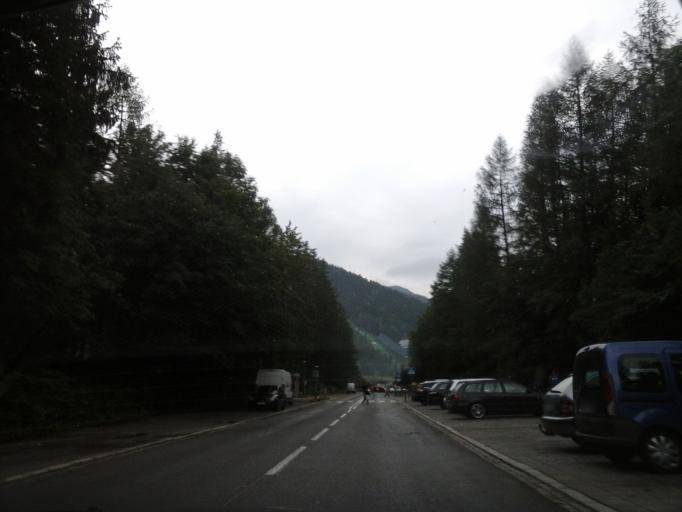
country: PL
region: Lesser Poland Voivodeship
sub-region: Powiat tatrzanski
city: Zakopane
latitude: 49.2838
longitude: 19.9725
